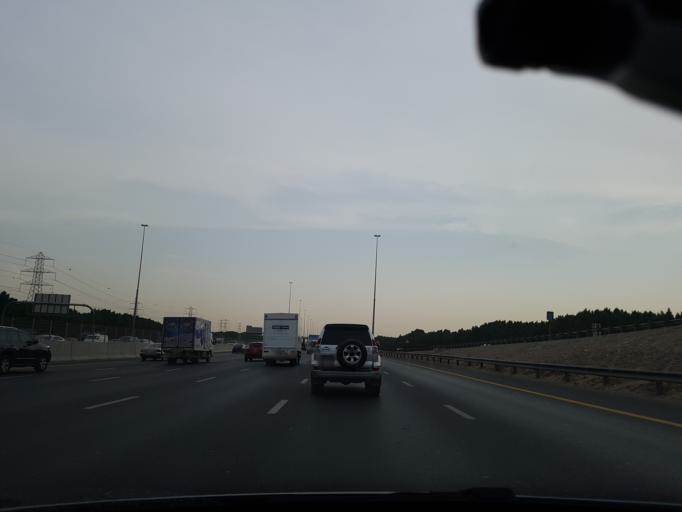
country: AE
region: Ash Shariqah
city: Sharjah
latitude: 25.2503
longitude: 55.4053
